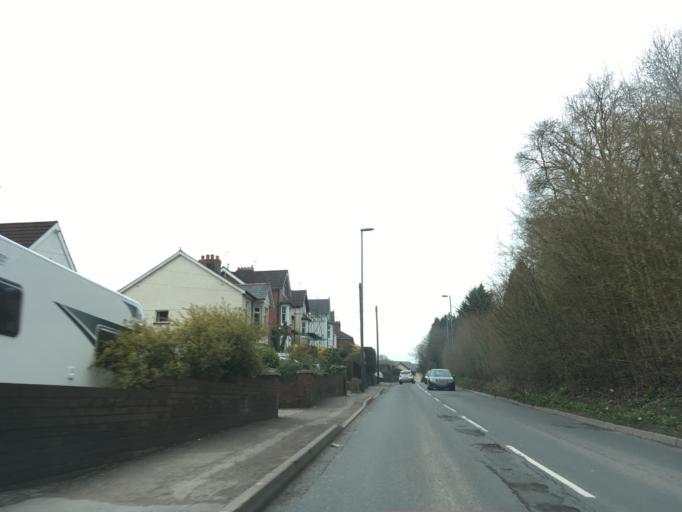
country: GB
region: Wales
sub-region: Newport
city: Caerleon
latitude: 51.6165
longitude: -2.9592
